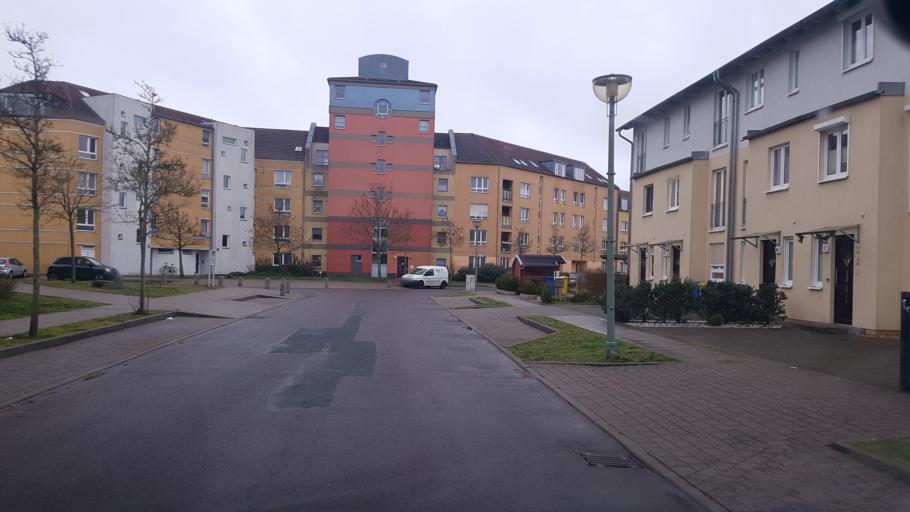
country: DE
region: Berlin
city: Wannsee
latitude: 52.3594
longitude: 13.1358
